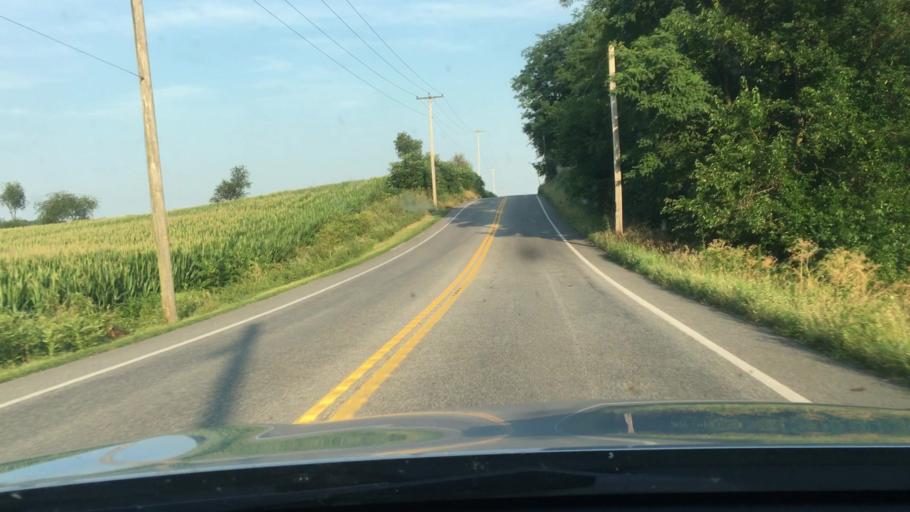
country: US
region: Pennsylvania
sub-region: Cumberland County
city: Boiling Springs
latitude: 40.1662
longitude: -77.1067
